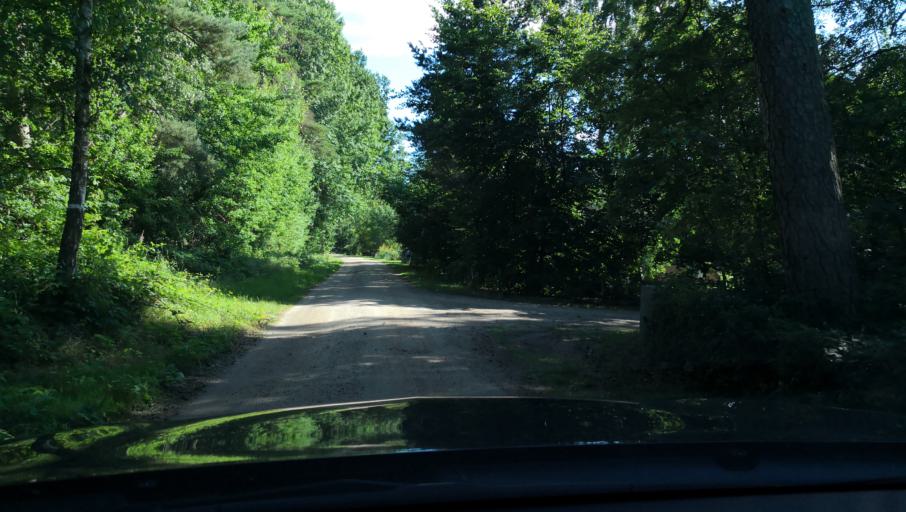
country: SE
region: Skane
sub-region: Kristianstads Kommun
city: Degeberga
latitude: 55.7954
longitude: 14.1955
